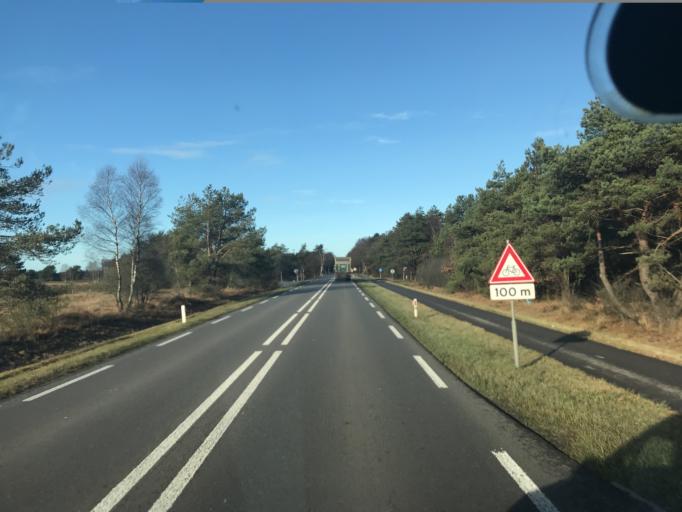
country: NL
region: Gelderland
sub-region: Gemeente Barneveld
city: Garderen
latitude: 52.2663
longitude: 5.7369
